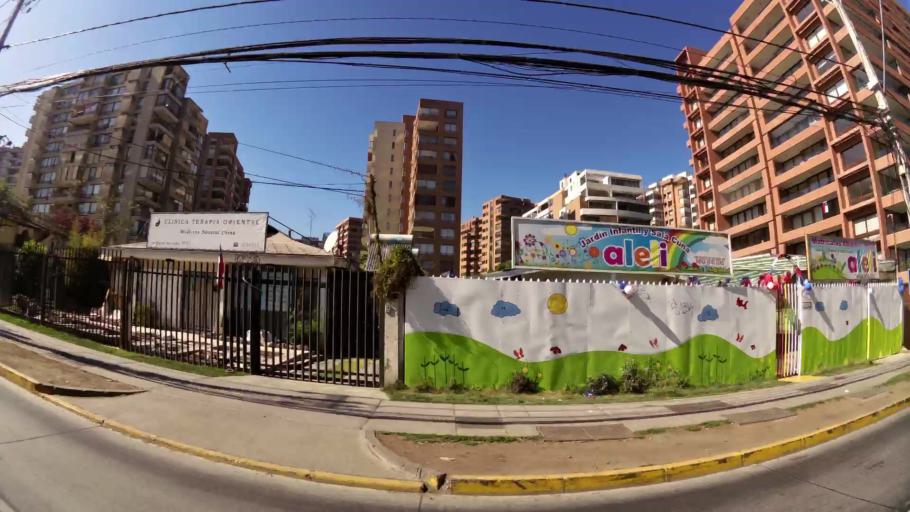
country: CL
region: Santiago Metropolitan
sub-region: Provincia de Santiago
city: Villa Presidente Frei, Nunoa, Santiago, Chile
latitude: -33.4042
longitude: -70.5663
